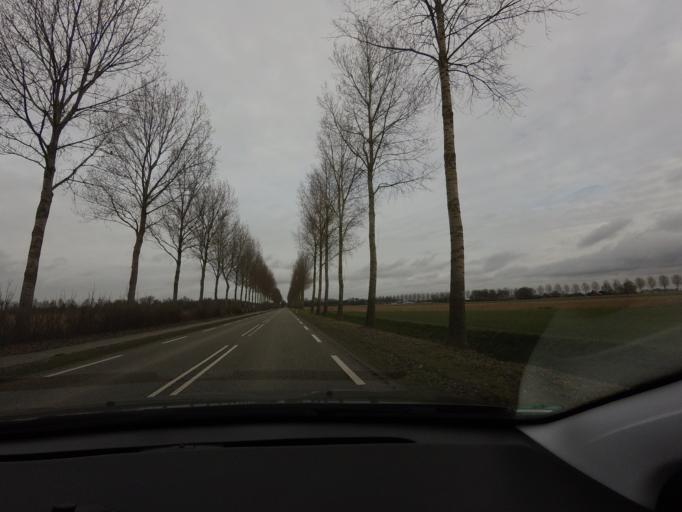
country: NL
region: Flevoland
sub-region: Gemeente Urk
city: Urk
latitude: 52.7559
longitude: 5.6522
